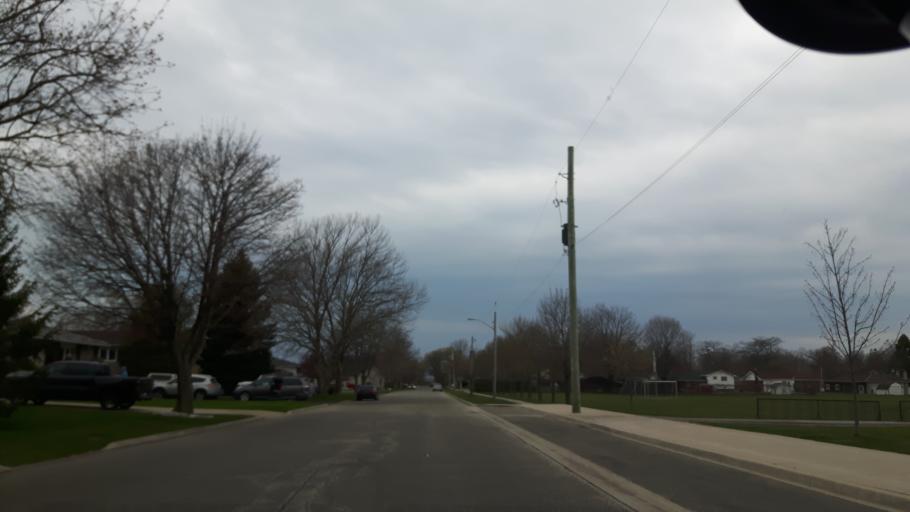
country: CA
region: Ontario
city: Goderich
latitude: 43.7336
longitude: -81.7173
